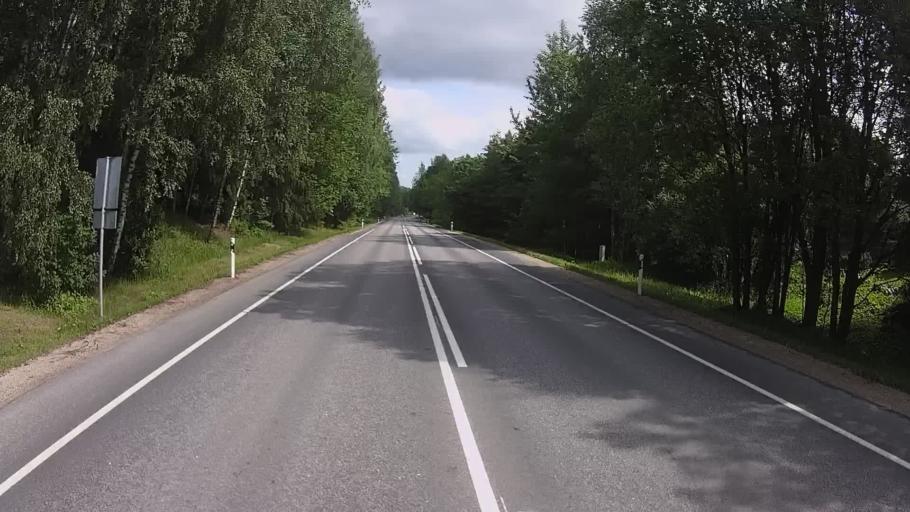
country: EE
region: Polvamaa
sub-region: Polva linn
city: Polva
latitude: 58.0634
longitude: 27.0545
